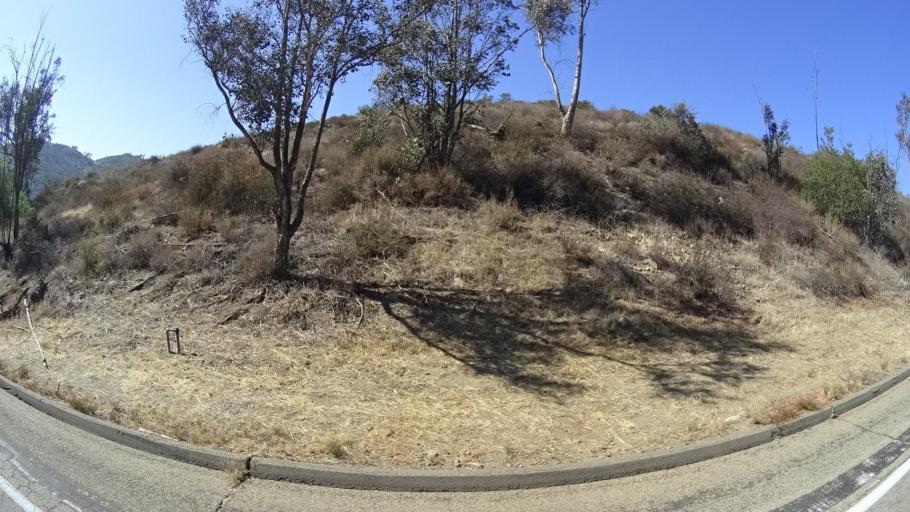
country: US
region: California
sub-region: San Diego County
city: Hidden Meadows
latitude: 33.2550
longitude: -117.1510
